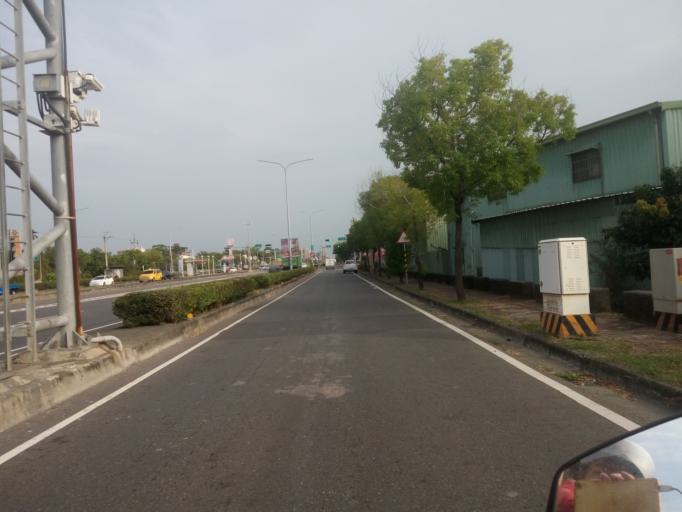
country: TW
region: Taiwan
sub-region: Chiayi
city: Jiayi Shi
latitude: 23.4845
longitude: 120.4114
